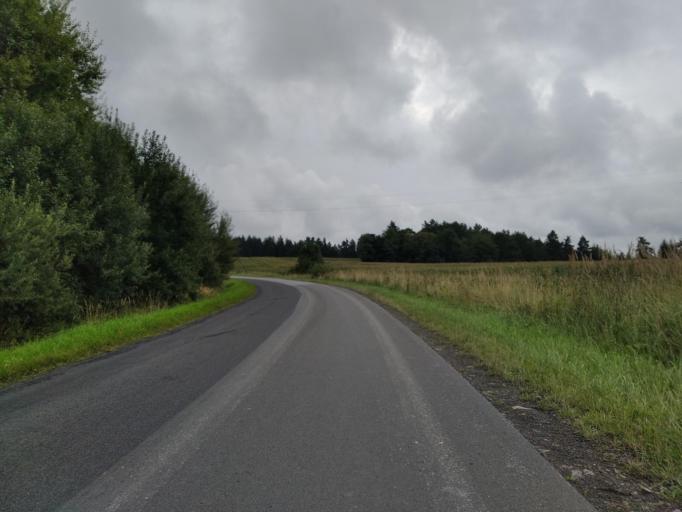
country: PL
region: Subcarpathian Voivodeship
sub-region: Powiat rzeszowski
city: Dynow
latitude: 49.7232
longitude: 22.3105
